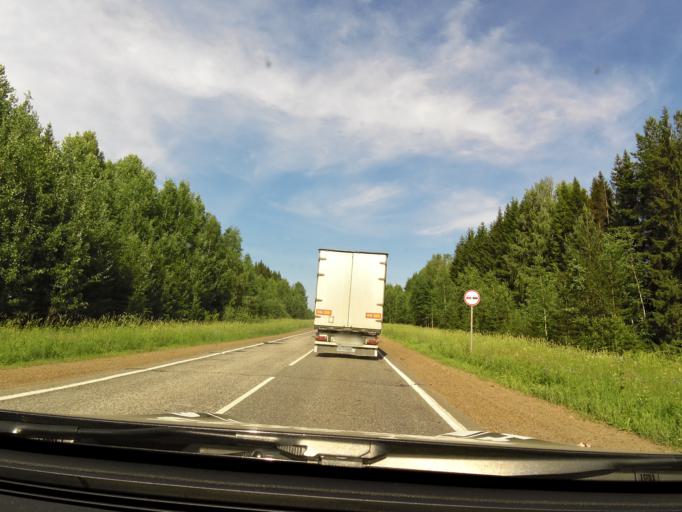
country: RU
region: Kirov
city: Belaya Kholunitsa
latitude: 58.8146
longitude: 50.5875
